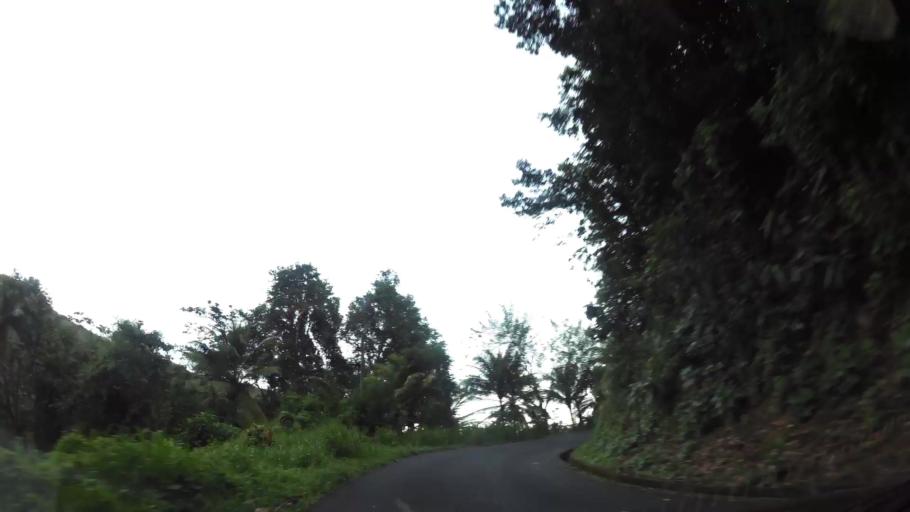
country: DM
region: Saint Andrew
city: Calibishie
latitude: 15.5928
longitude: -61.3576
